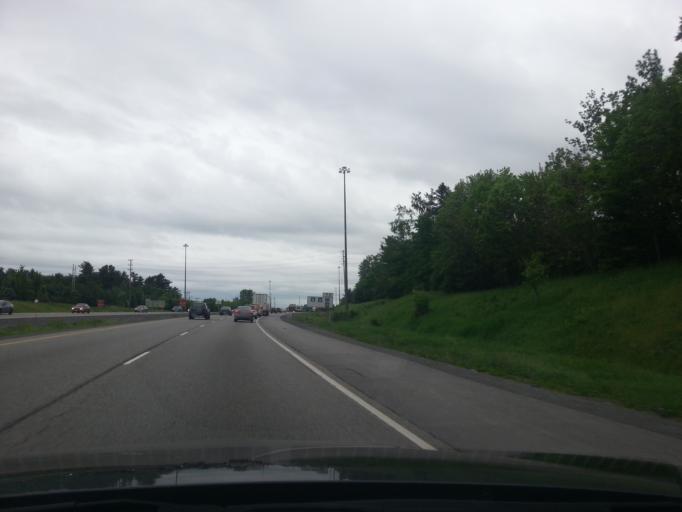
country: CA
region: Ontario
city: Bells Corners
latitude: 45.3251
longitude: -75.8062
